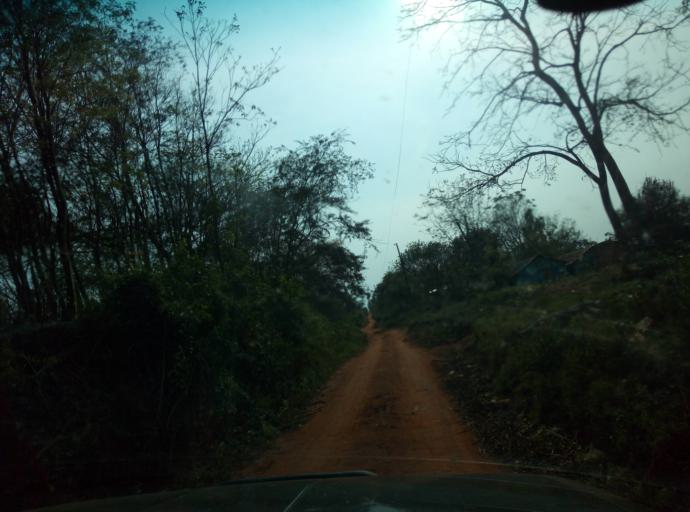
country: PY
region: Caaguazu
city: San Joaquin
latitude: -25.1503
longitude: -56.1024
